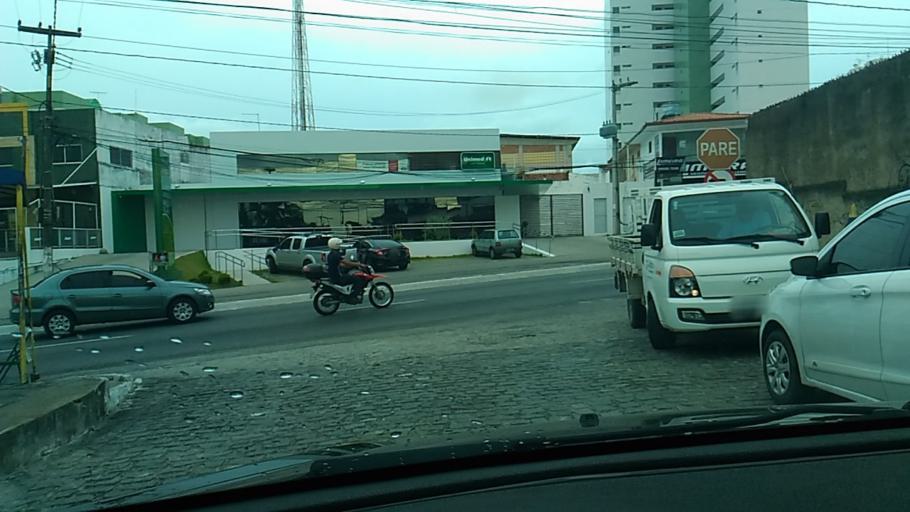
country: BR
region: Paraiba
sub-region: Joao Pessoa
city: Joao Pessoa
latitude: -7.1517
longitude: -34.8394
